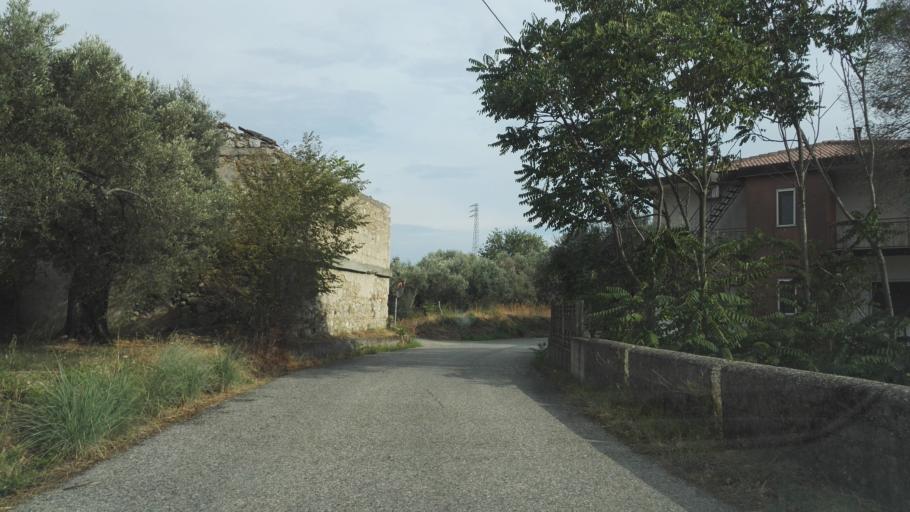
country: IT
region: Calabria
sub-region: Provincia di Reggio Calabria
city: Stignano
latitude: 38.4258
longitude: 16.4648
